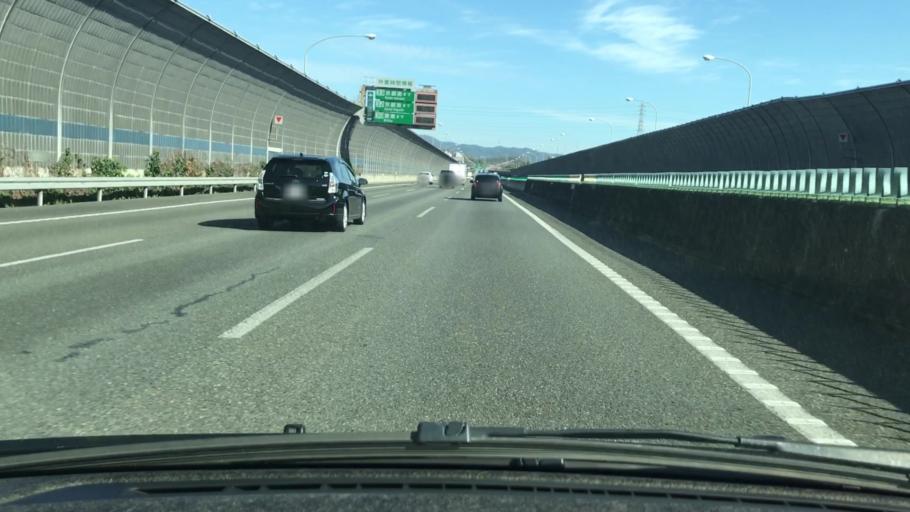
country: JP
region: Osaka
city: Ibaraki
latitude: 34.8379
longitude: 135.5669
